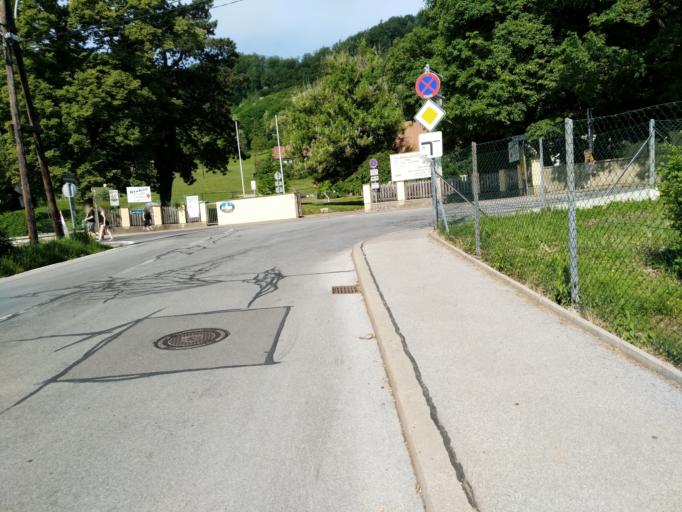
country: AT
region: Styria
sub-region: Graz Stadt
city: Wetzelsdorf
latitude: 47.0466
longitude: 15.3871
